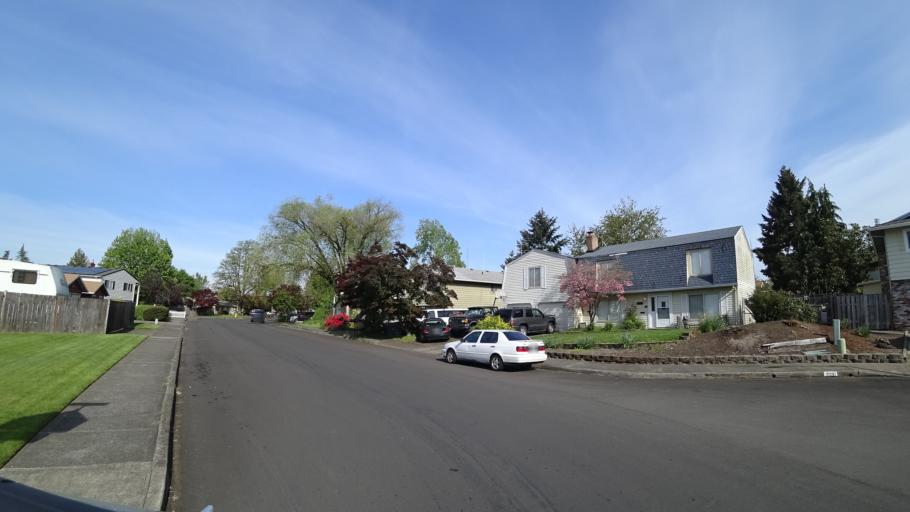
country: US
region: Oregon
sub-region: Washington County
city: Hillsboro
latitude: 45.5258
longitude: -122.9613
